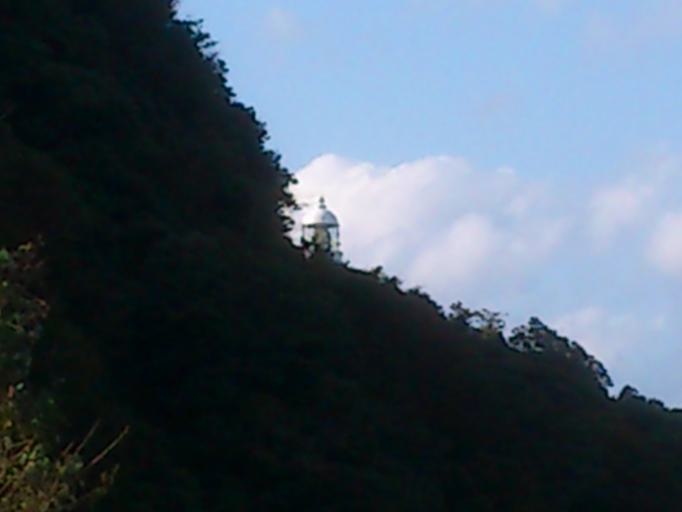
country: JP
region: Kyoto
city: Miyazu
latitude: 35.7741
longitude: 135.2252
